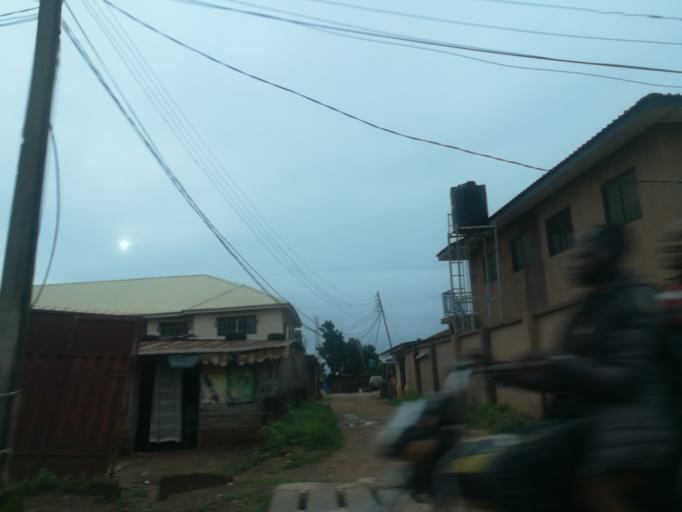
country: NG
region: Oyo
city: Egbeda
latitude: 7.3996
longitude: 3.9783
